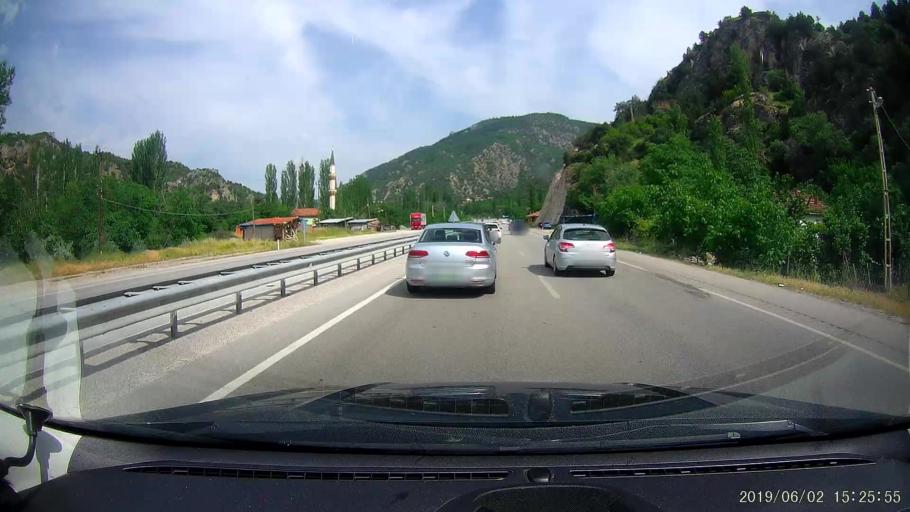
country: TR
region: Amasya
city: Saraycik
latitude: 40.9897
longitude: 35.0282
